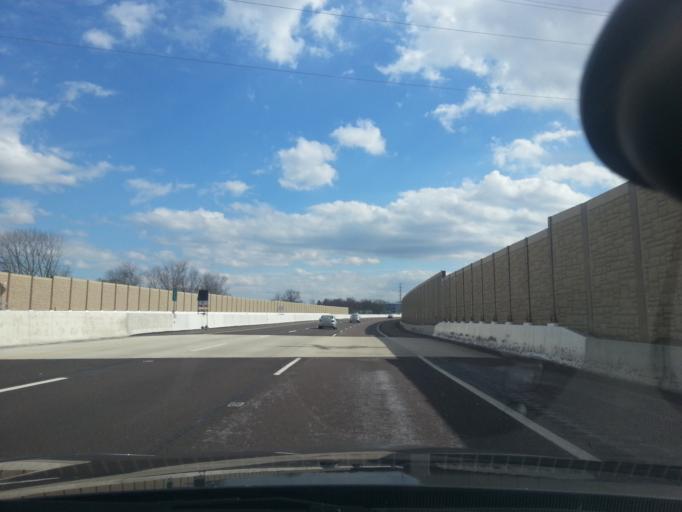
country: US
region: Pennsylvania
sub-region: Montgomery County
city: Blue Bell
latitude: 40.1545
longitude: -75.2943
